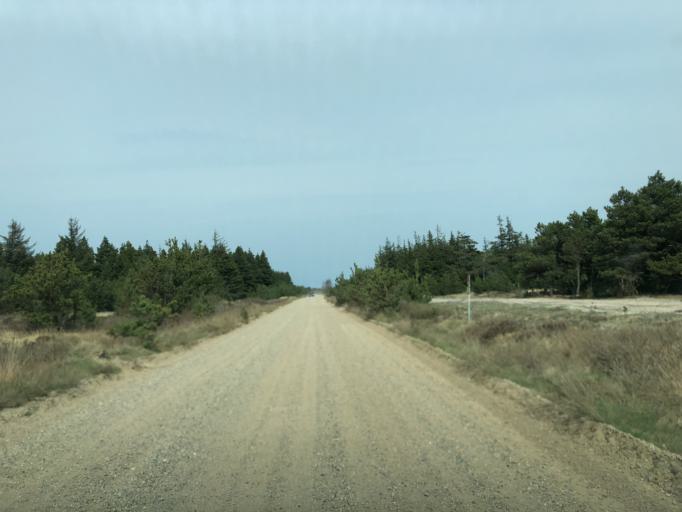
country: DK
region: South Denmark
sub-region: Varde Kommune
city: Oksbol
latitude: 55.6033
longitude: 8.1584
